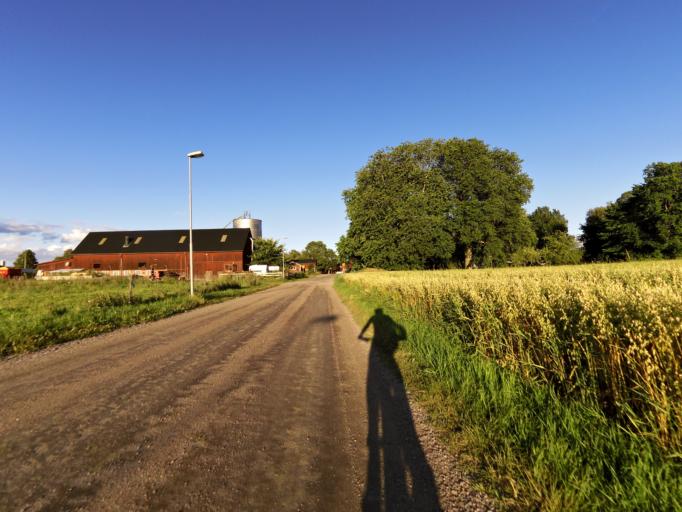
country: SE
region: Gaevleborg
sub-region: Gavle Kommun
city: Gavle
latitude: 60.7195
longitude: 17.1605
